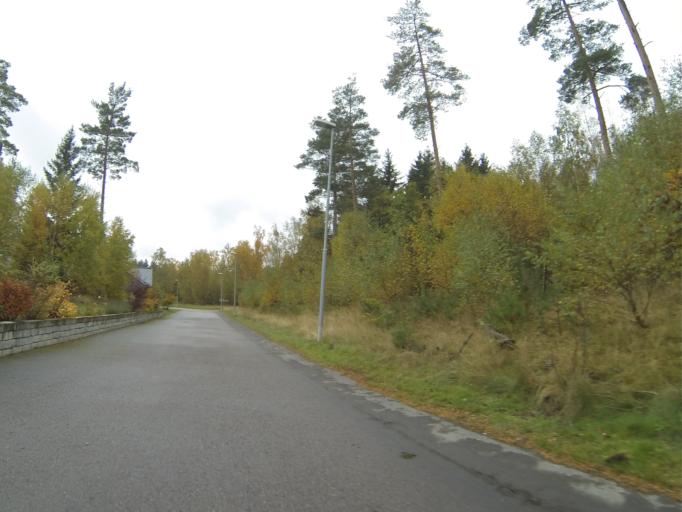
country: SE
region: Skane
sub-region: Sjobo Kommun
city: Sjoebo
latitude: 55.6380
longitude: 13.6675
